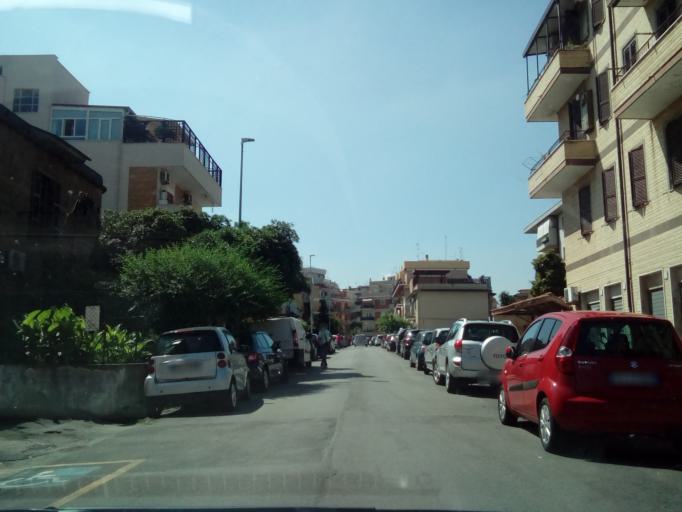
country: IT
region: Latium
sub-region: Citta metropolitana di Roma Capitale
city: Rome
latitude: 41.8746
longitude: 12.5782
